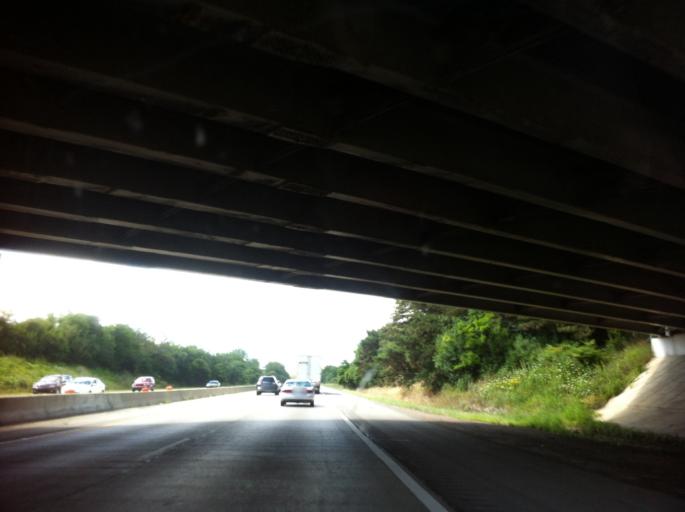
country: US
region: Michigan
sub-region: Washtenaw County
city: Ann Arbor
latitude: 42.2318
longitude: -83.6988
